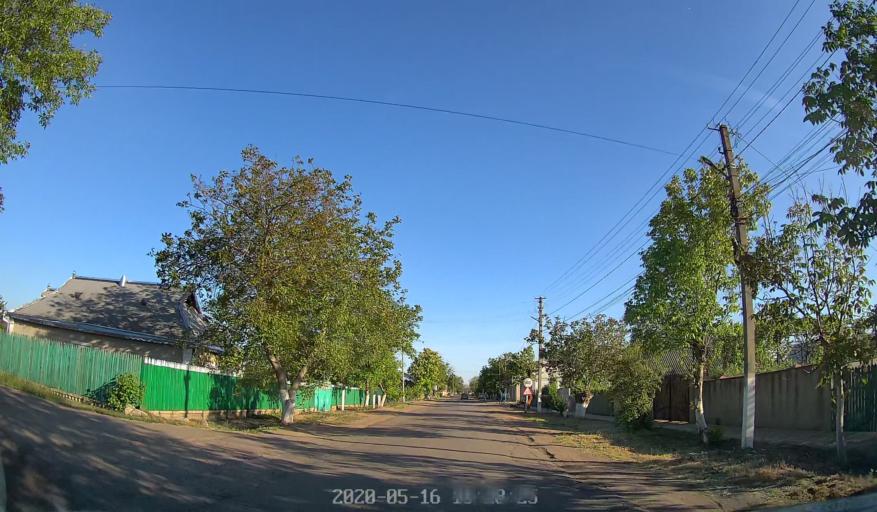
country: MD
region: Telenesti
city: Dnestrovsc
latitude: 46.5399
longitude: 30.0143
